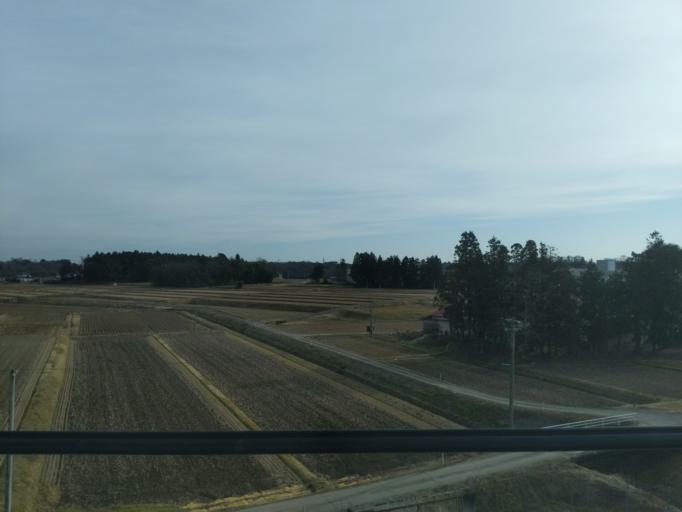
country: JP
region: Iwate
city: Ichinoseki
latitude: 38.7436
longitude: 141.0687
